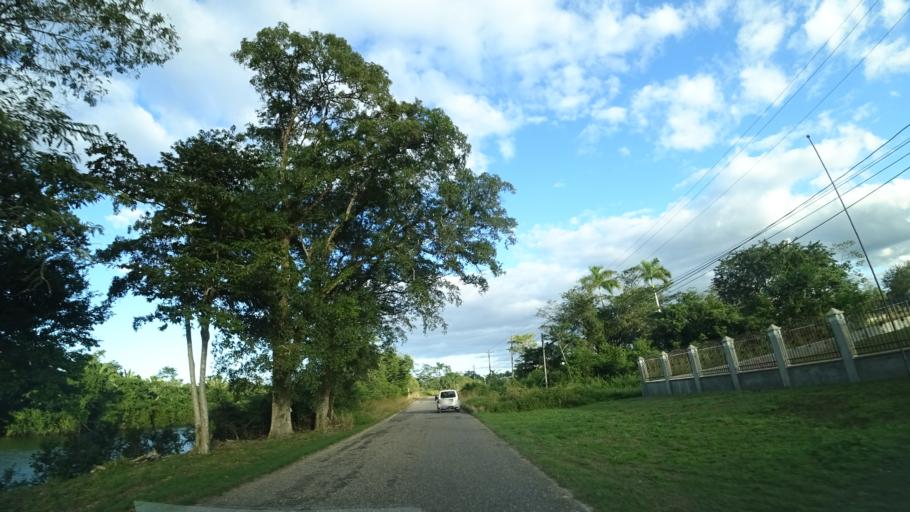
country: BZ
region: Belize
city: Belize City
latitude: 17.5717
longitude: -88.3921
